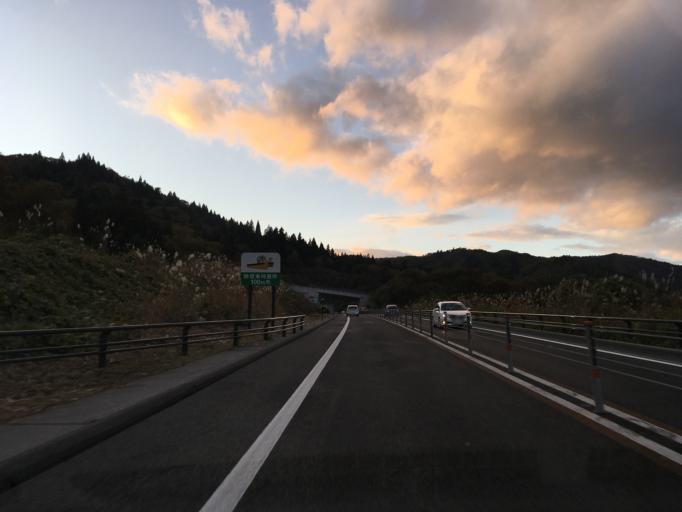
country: JP
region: Iwate
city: Kitakami
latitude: 39.2922
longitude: 141.3172
